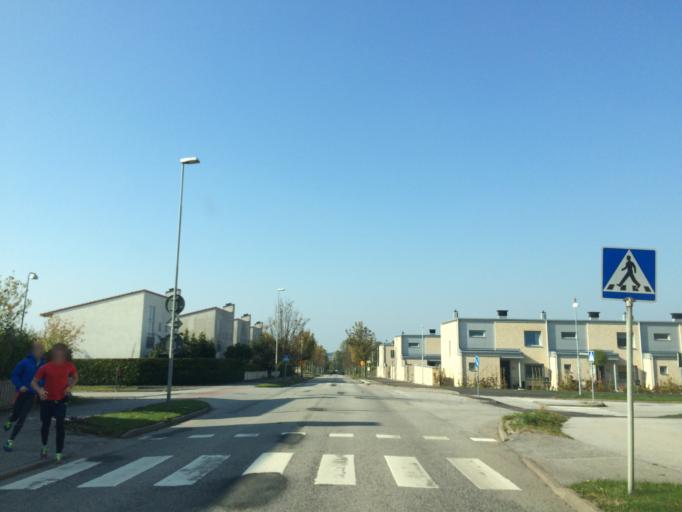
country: SE
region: Skane
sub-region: Staffanstorps Kommun
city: Hjaerup
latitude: 55.7036
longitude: 13.1542
